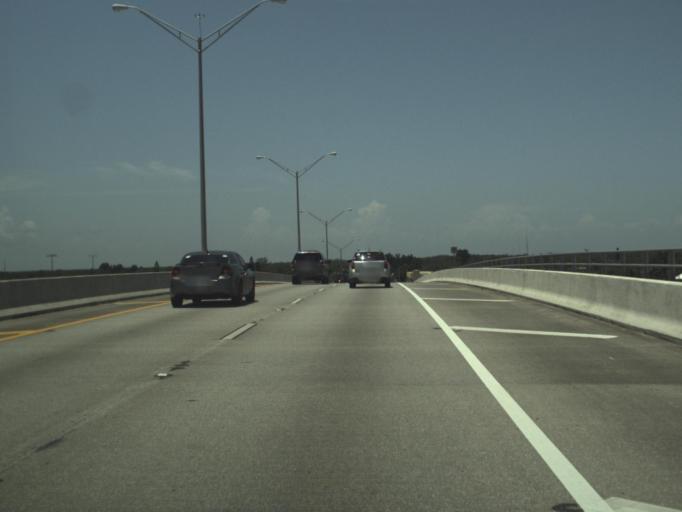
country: US
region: Florida
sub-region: Martin County
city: Palm City
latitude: 27.1744
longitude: -80.2606
